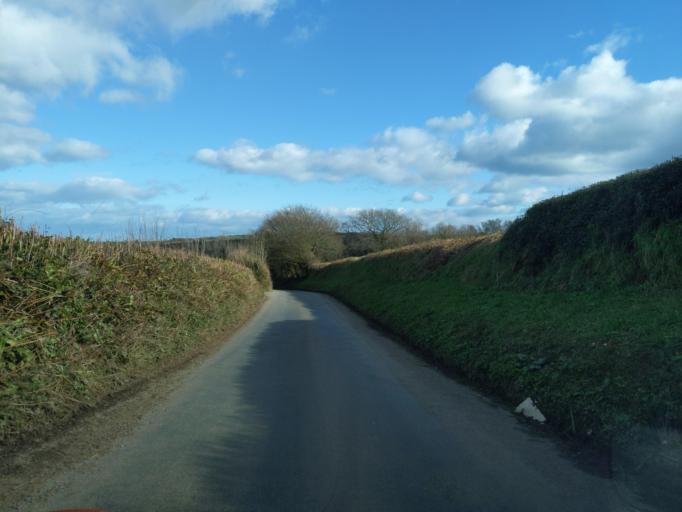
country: GB
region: England
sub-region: Devon
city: Salcombe
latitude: 50.2571
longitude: -3.7074
